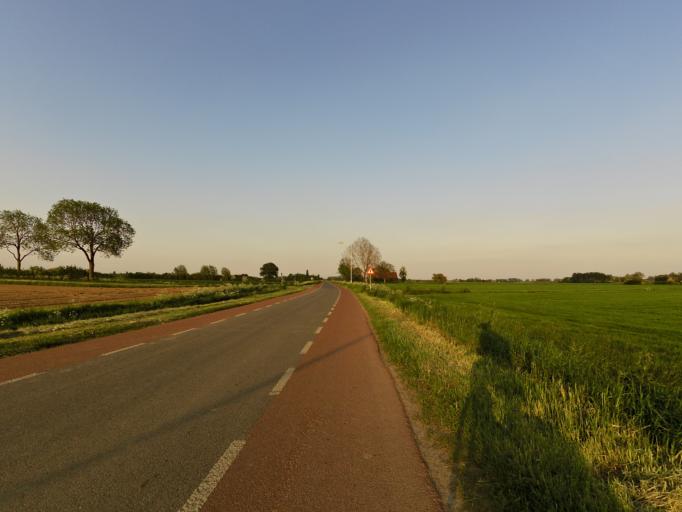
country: NL
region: Gelderland
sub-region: Oude IJsselstreek
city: Gendringen
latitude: 51.8586
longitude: 6.3176
